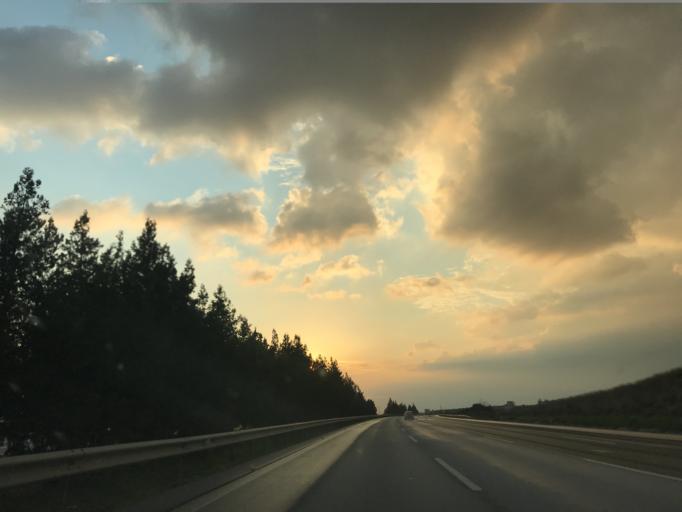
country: TR
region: Mersin
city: Yenice
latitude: 37.0378
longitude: 35.1436
